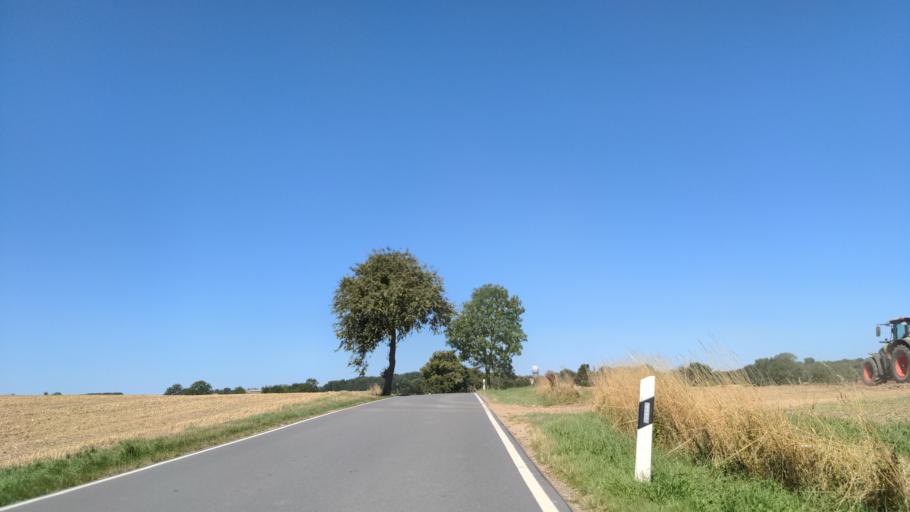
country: DE
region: Mecklenburg-Vorpommern
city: Klutz
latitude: 53.9871
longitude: 11.1301
